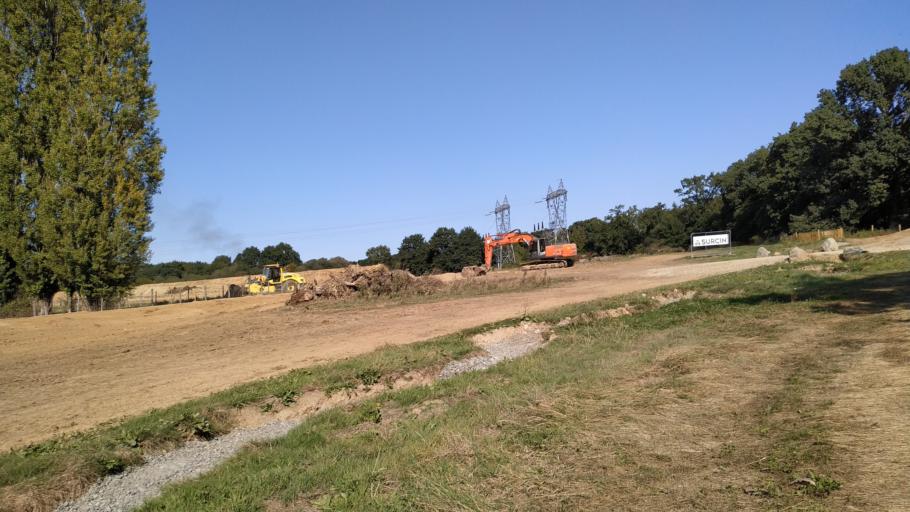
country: FR
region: Brittany
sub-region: Departement d'Ille-et-Vilaine
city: Cesson-Sevigne
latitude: 48.1291
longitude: -1.6061
